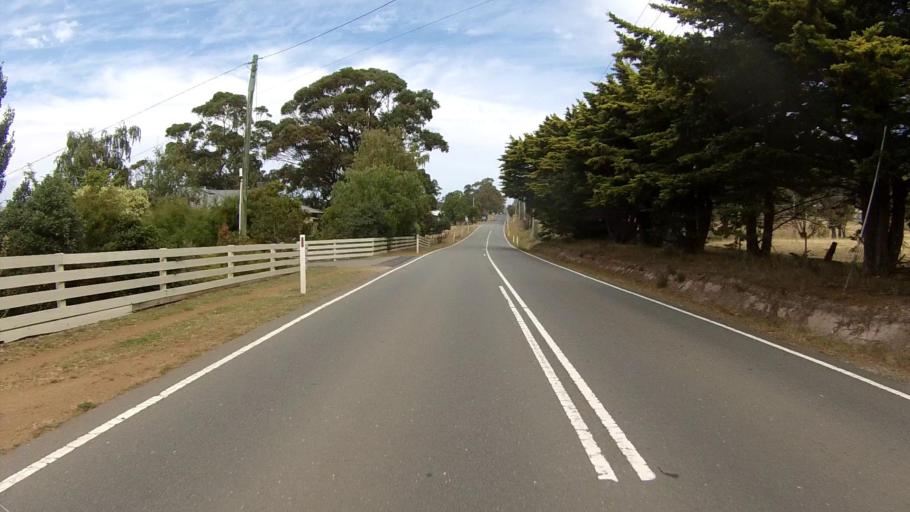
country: AU
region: Tasmania
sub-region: Clarence
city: Acton Park
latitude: -42.8931
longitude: 147.4819
